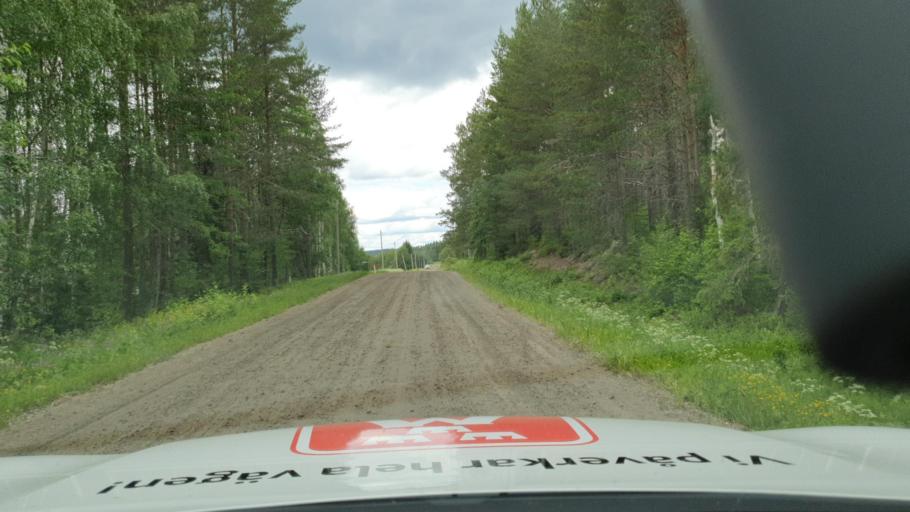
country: SE
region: Vaesterbotten
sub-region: Bjurholms Kommun
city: Bjurholm
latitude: 63.8261
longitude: 19.0152
